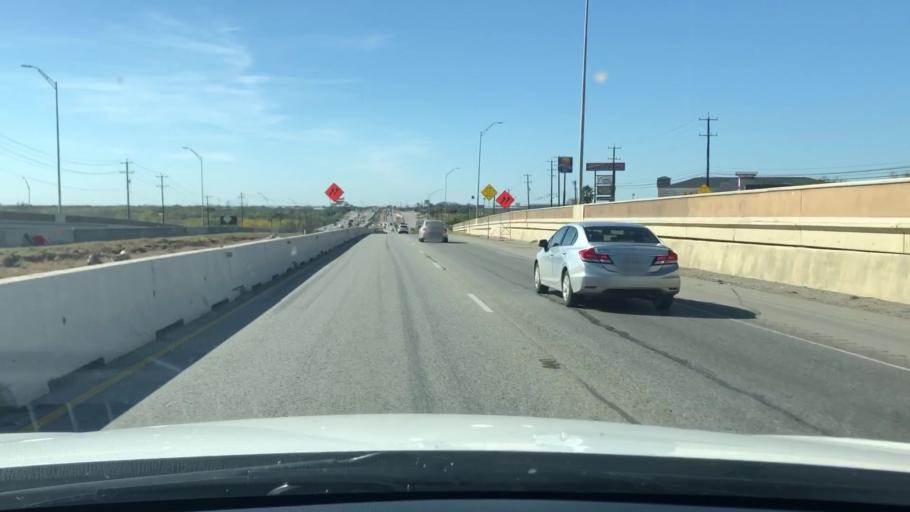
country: US
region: Texas
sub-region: Bexar County
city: Kirby
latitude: 29.4432
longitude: -98.3644
